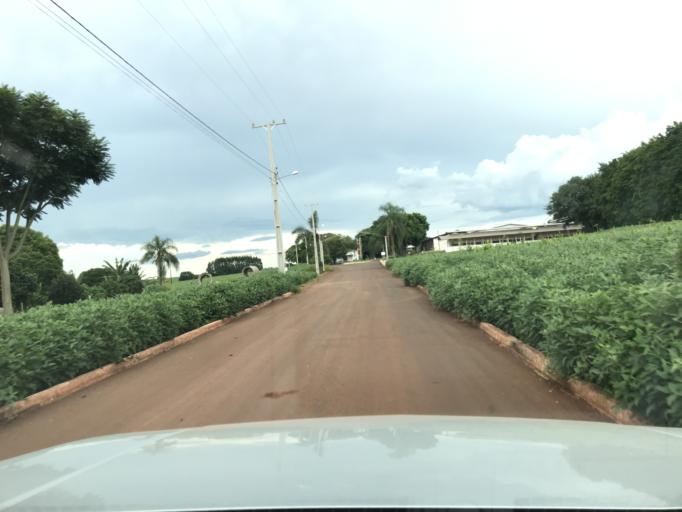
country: BR
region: Parana
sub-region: Palotina
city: Palotina
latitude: -24.2789
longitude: -53.7920
